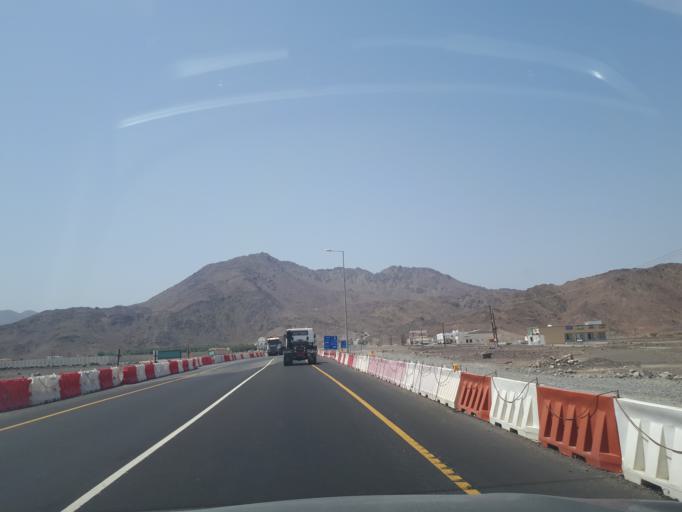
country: OM
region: Muhafazat ad Dakhiliyah
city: Sufalat Sama'il
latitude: 23.2594
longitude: 58.1036
